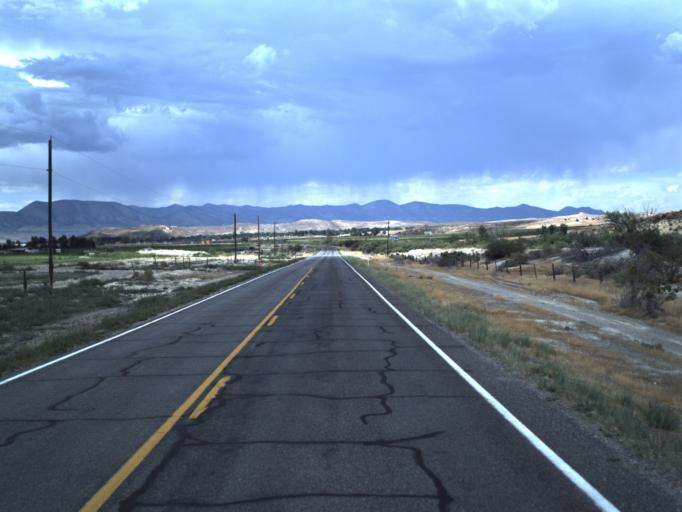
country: US
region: Utah
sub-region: Sanpete County
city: Centerfield
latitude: 39.1362
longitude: -111.7792
